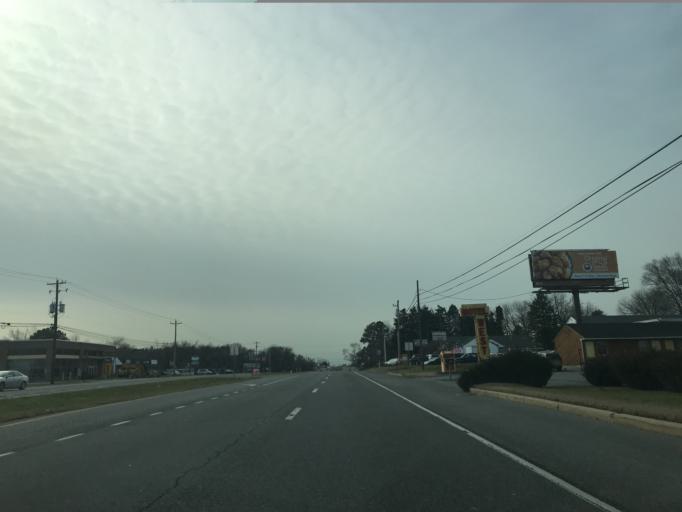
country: US
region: Delaware
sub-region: New Castle County
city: Bear
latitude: 39.6458
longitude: -75.6374
